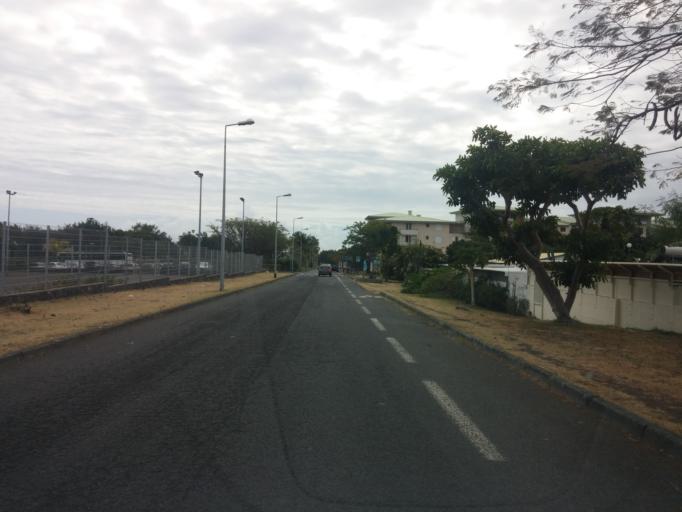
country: RE
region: Reunion
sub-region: Reunion
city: Le Port
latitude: -20.9502
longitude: 55.2941
